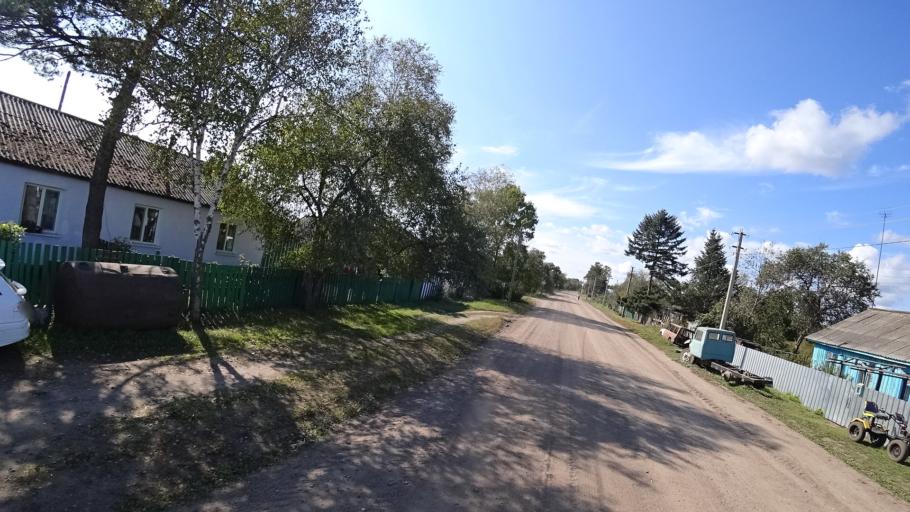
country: RU
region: Amur
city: Arkhara
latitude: 49.4019
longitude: 130.1487
